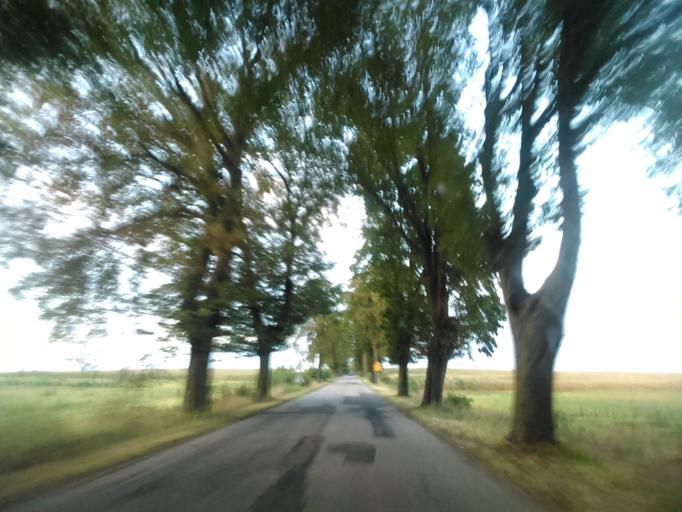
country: PL
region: Kujawsko-Pomorskie
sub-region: Powiat wabrzeski
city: Debowa Laka
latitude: 53.1957
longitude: 19.1600
